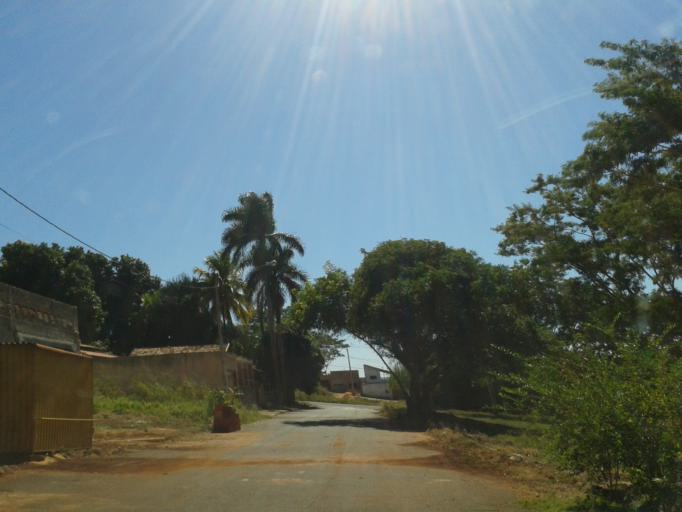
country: BR
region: Minas Gerais
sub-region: Capinopolis
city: Capinopolis
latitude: -18.5183
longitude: -49.4986
